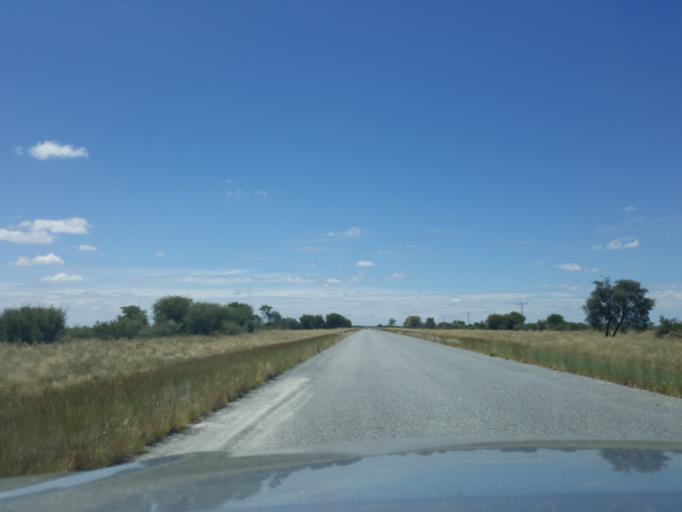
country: BW
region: Central
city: Nata
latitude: -20.1985
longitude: 26.1082
